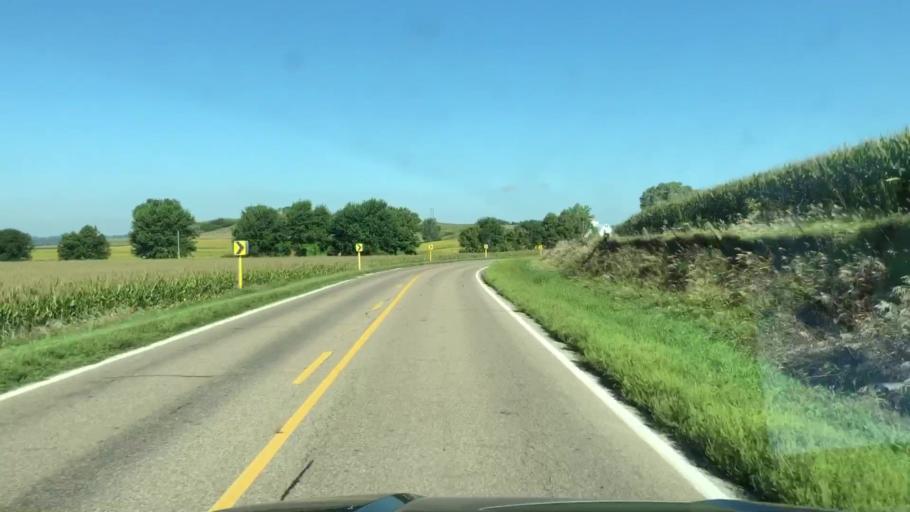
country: US
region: Iowa
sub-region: Woodbury County
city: Sergeant Bluff
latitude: 42.4084
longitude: -96.2550
